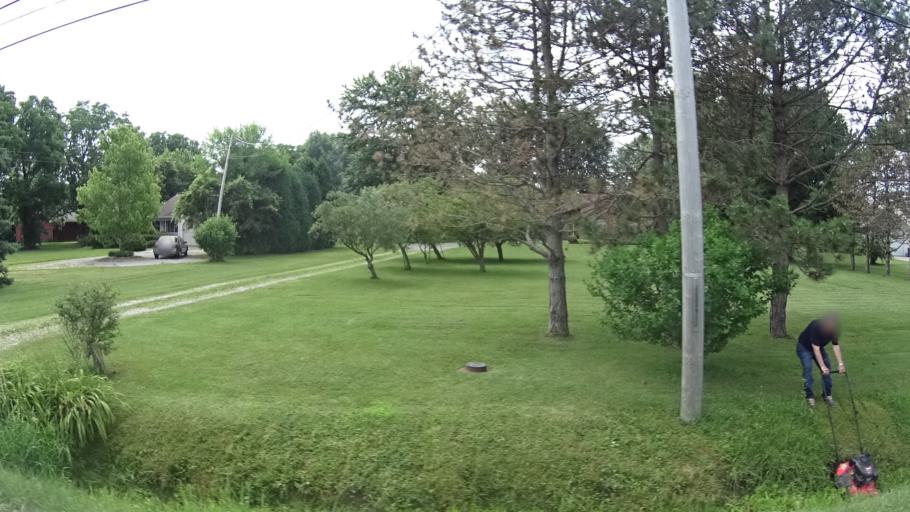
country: US
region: Ohio
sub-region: Lorain County
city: Vermilion
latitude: 41.3694
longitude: -82.3503
